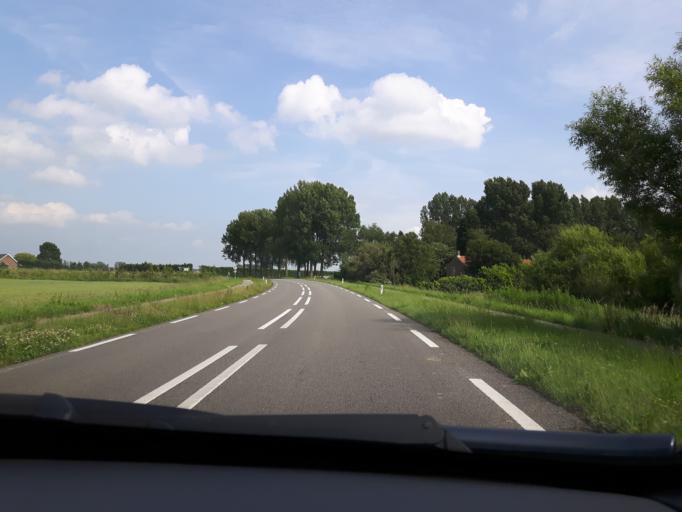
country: NL
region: Zeeland
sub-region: Gemeente Borsele
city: Borssele
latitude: 51.4974
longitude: 3.7289
